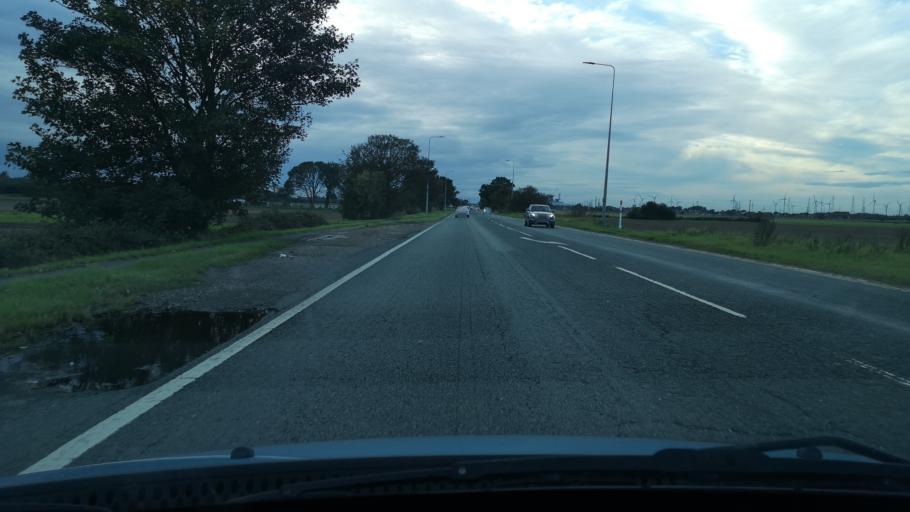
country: GB
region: England
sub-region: North Lincolnshire
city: Gunness
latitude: 53.5897
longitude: -0.7045
